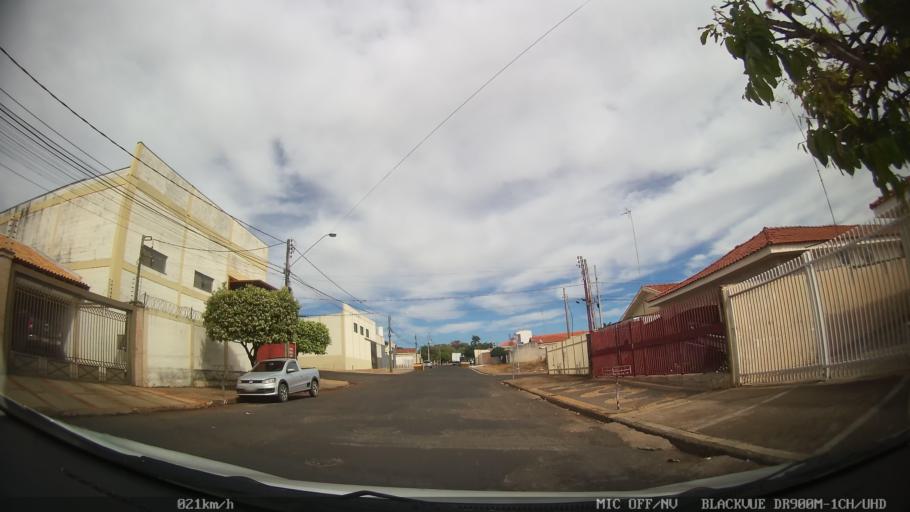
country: BR
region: Sao Paulo
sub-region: Catanduva
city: Catanduva
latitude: -21.1552
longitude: -48.9762
